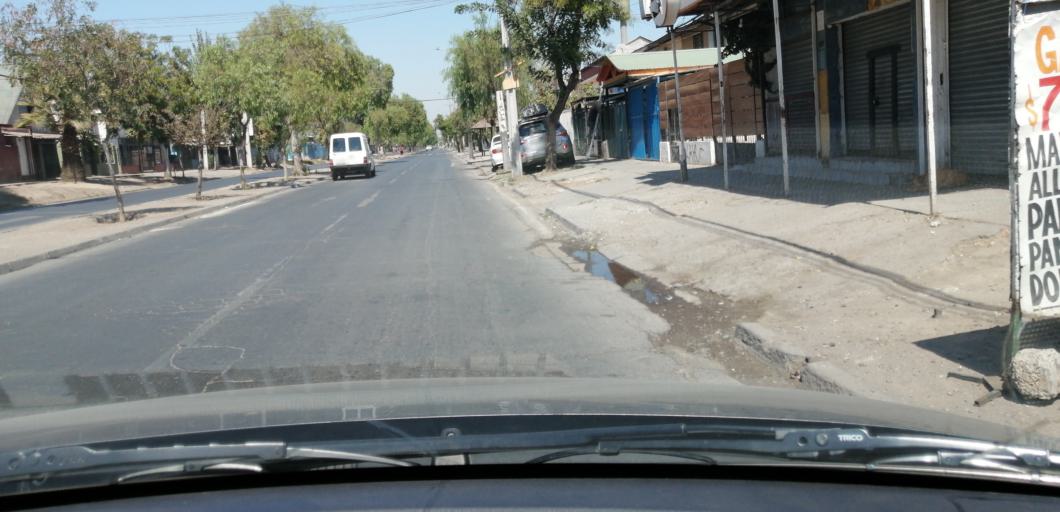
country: CL
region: Santiago Metropolitan
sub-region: Provincia de Santiago
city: Lo Prado
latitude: -33.4314
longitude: -70.7409
